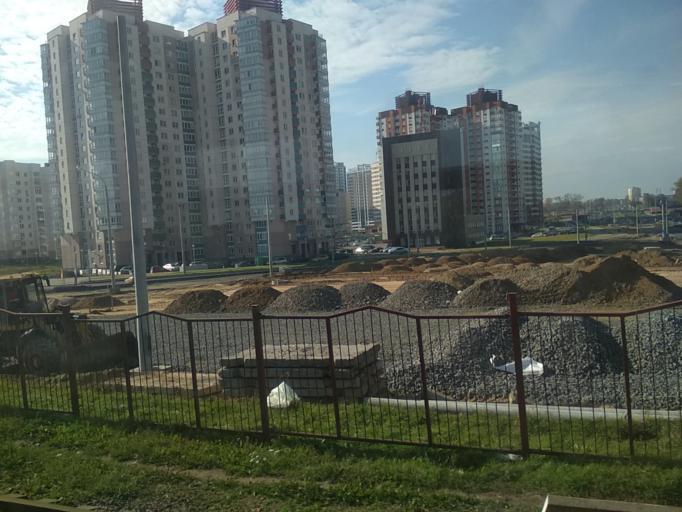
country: BY
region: Minsk
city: Minsk
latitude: 53.8715
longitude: 27.5616
